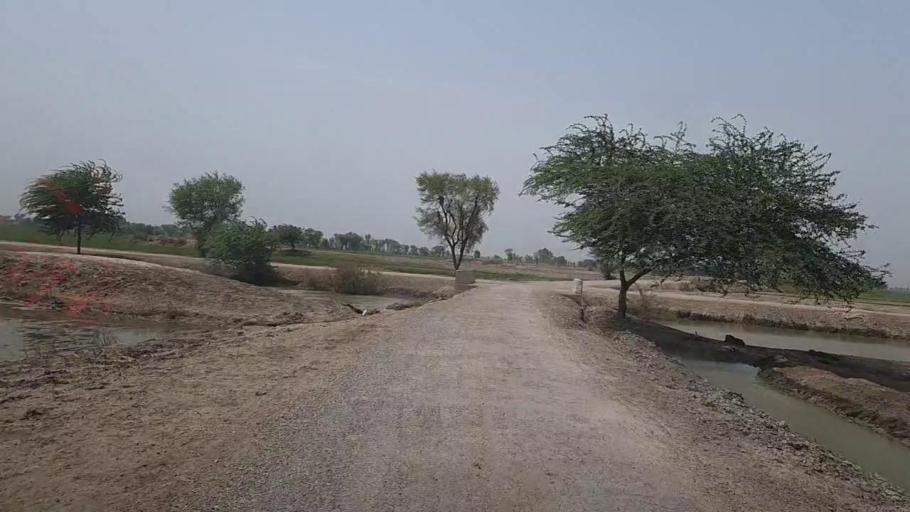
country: PK
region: Sindh
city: Sita Road
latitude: 27.0908
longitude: 67.8560
